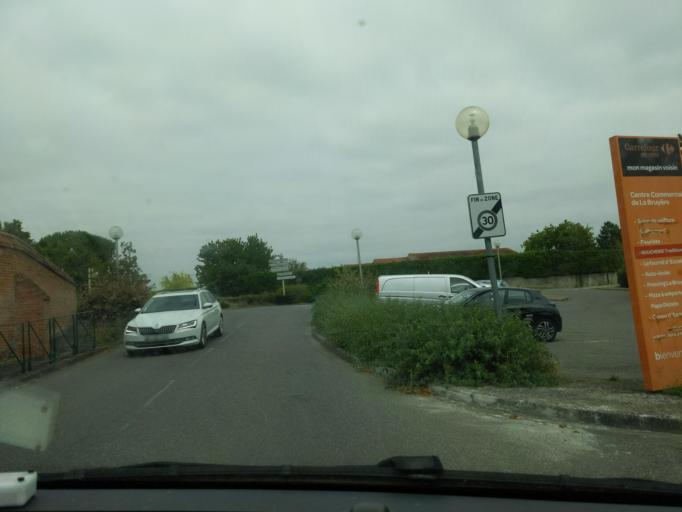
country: FR
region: Midi-Pyrenees
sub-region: Departement de la Haute-Garonne
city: Escalquens
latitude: 43.5181
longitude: 1.5618
